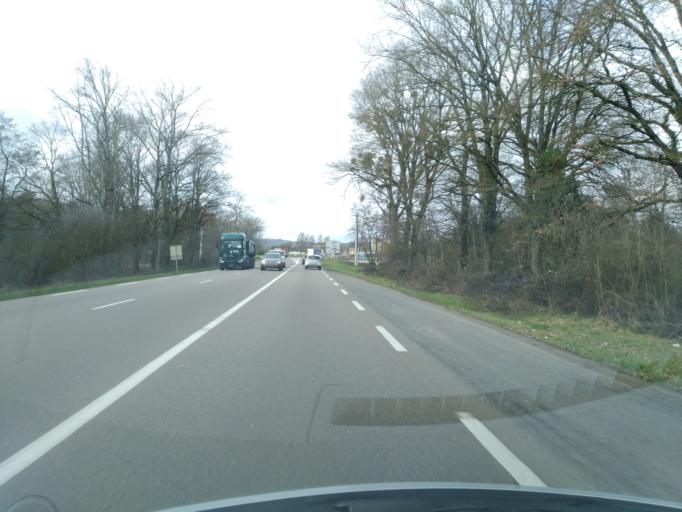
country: FR
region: Bourgogne
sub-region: Departement de Saone-et-Loire
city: Torcy
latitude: 46.7660
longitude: 4.4552
